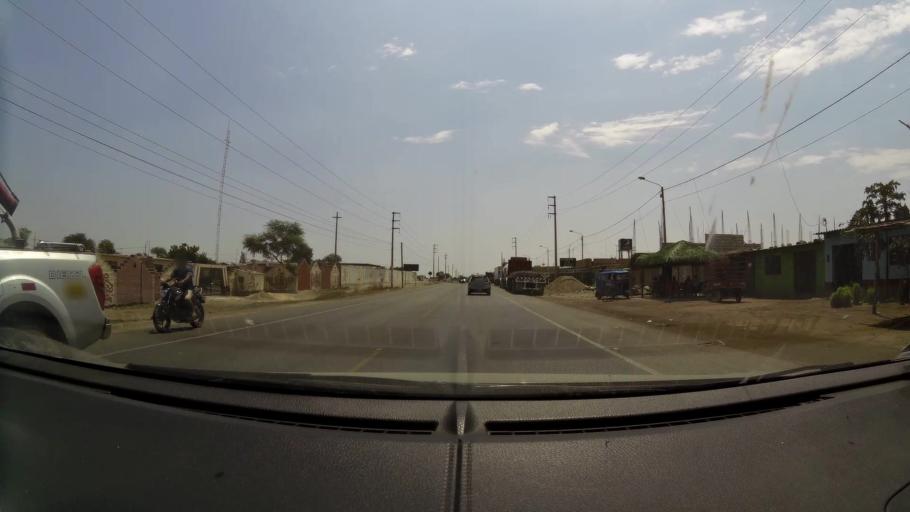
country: PE
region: La Libertad
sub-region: Chepen
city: Chepen
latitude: -7.1817
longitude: -79.4348
